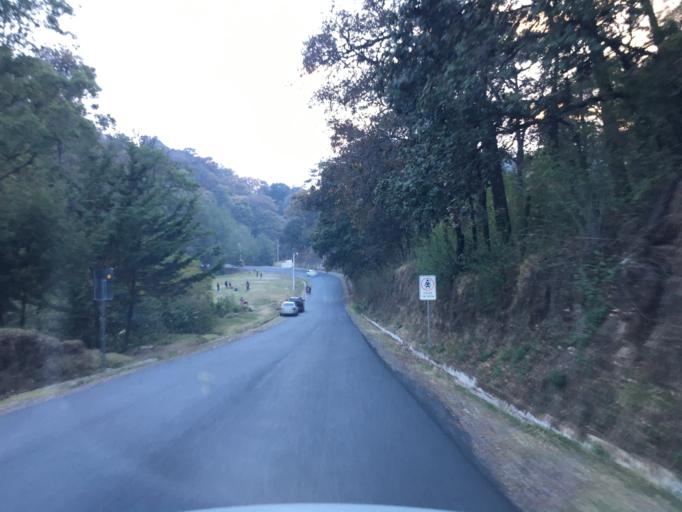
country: GT
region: Chimaltenango
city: Tecpan Guatemala
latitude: 14.7436
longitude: -91.0053
